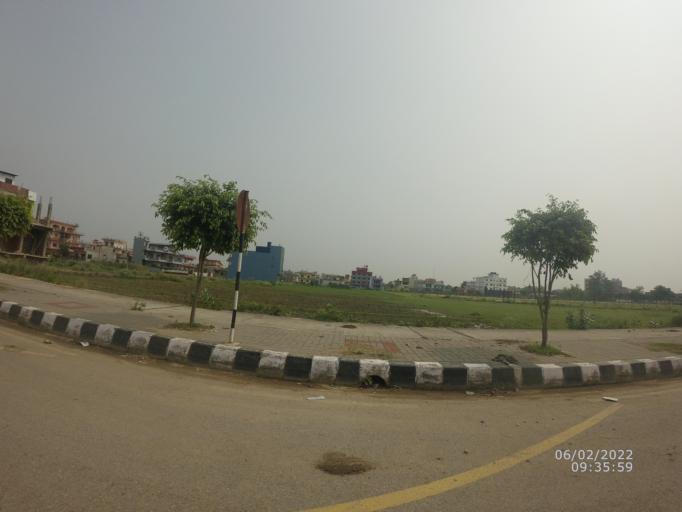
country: NP
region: Western Region
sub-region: Lumbini Zone
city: Bhairahawa
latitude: 27.4977
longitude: 83.4556
